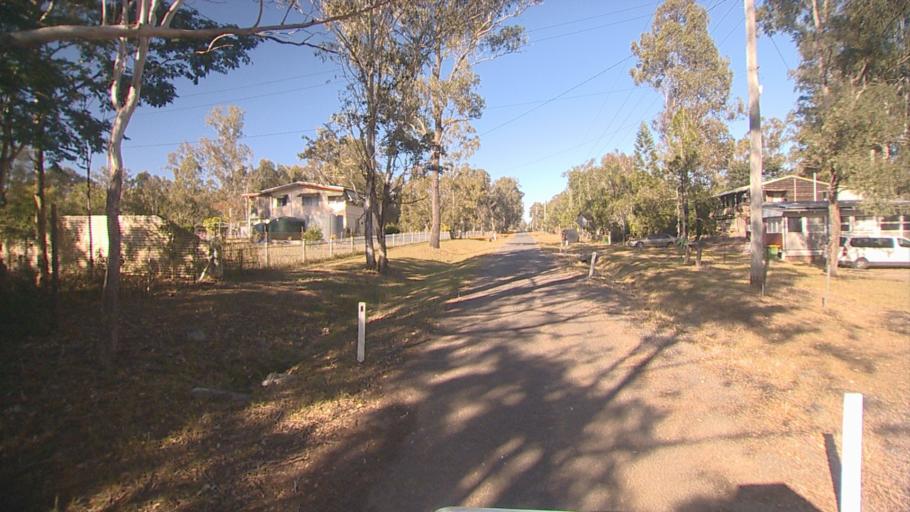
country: AU
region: Queensland
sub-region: Logan
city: Park Ridge South
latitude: -27.7499
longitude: 153.0347
